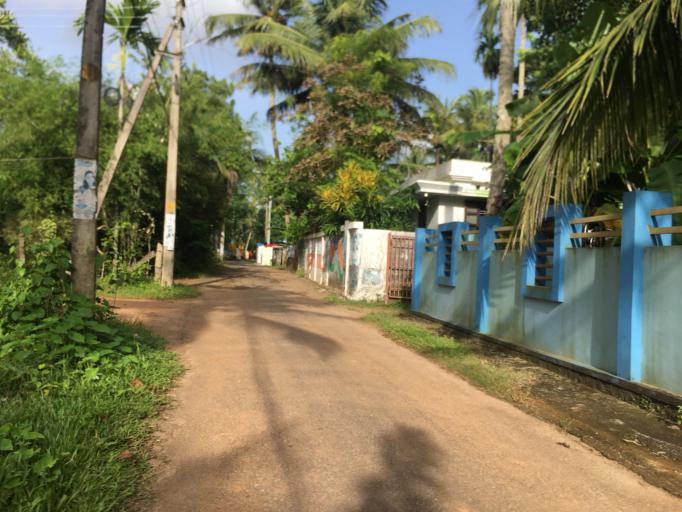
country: IN
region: Kerala
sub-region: Alappuzha
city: Kattanam
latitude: 9.1967
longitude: 76.5341
